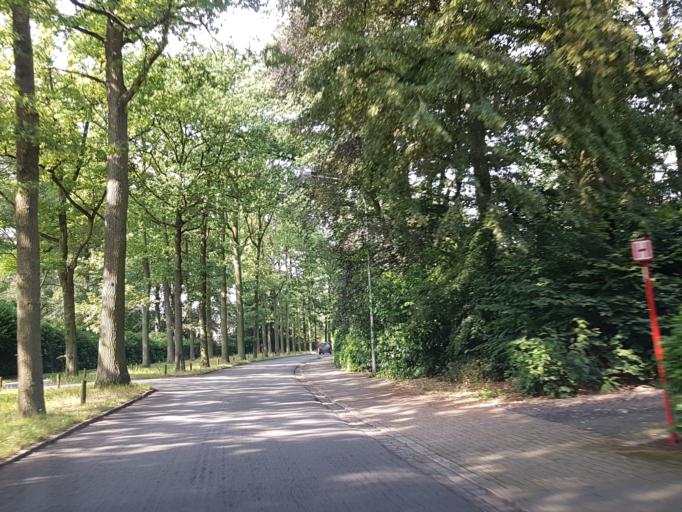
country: BE
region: Flanders
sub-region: Provincie Antwerpen
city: Brasschaat
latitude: 51.2824
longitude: 4.4705
